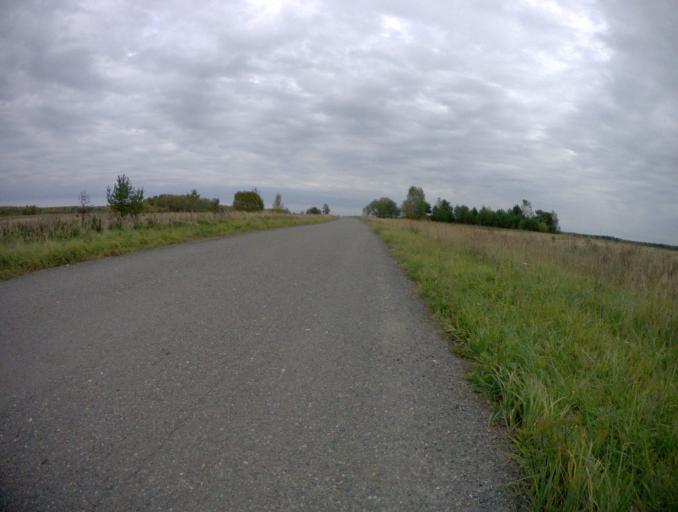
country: RU
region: Vladimir
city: Mstera
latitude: 56.3701
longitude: 41.7576
